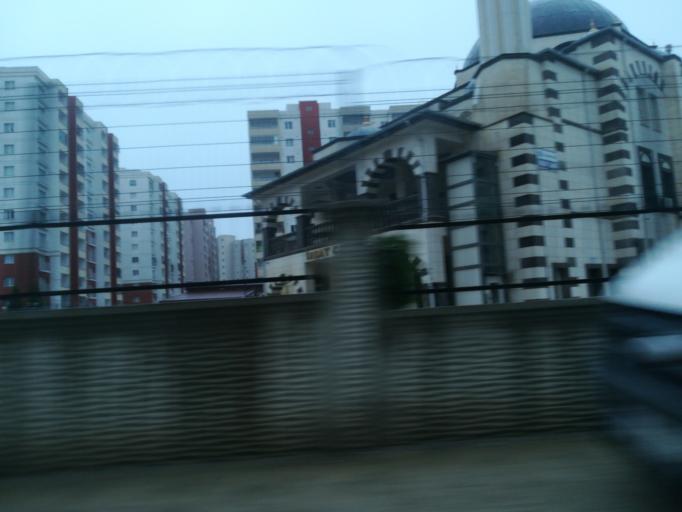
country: TR
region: Adana
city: Seyhan
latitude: 37.0083
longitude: 35.2773
